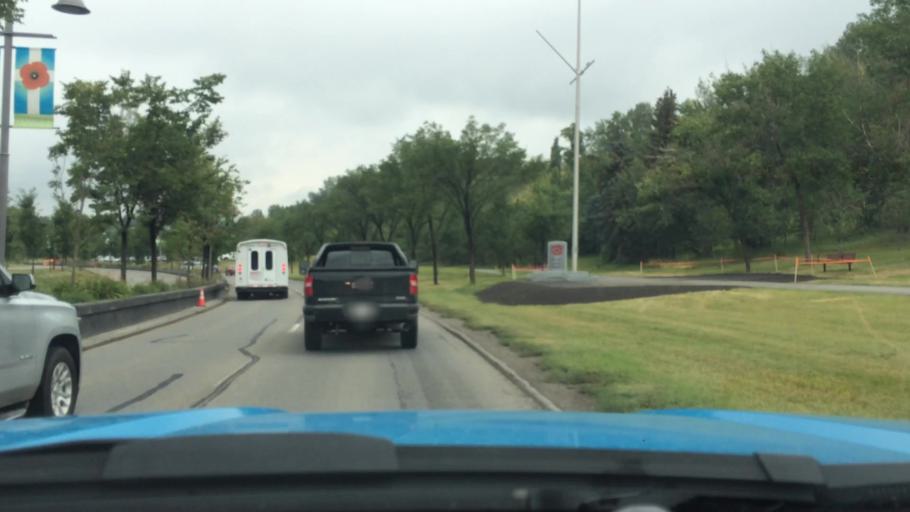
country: CA
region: Alberta
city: Calgary
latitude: 51.0562
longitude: -114.0649
